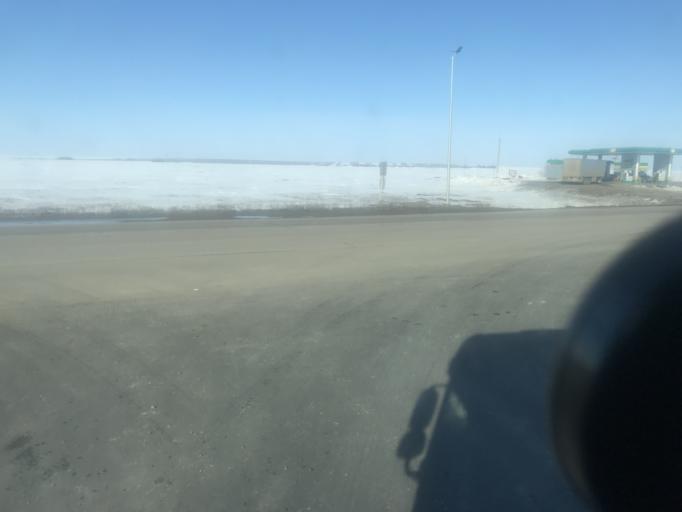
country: RU
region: Orenburg
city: Dombarovskiy
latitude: 49.9689
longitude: 60.0654
